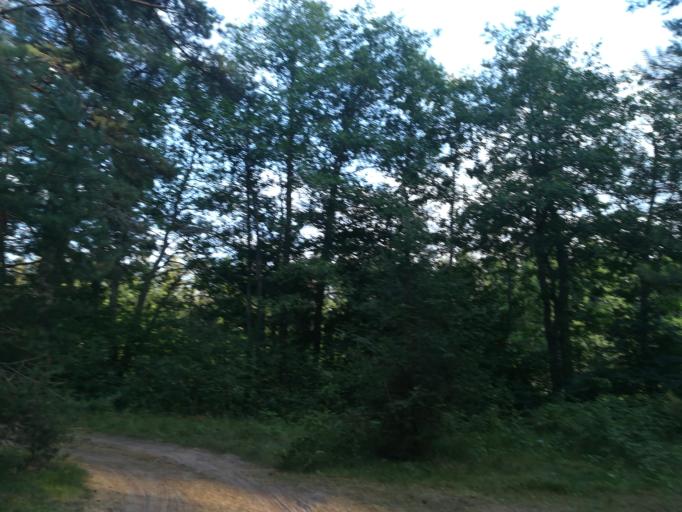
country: RU
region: Leningrad
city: Ust'-Luga
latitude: 59.6775
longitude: 28.2391
